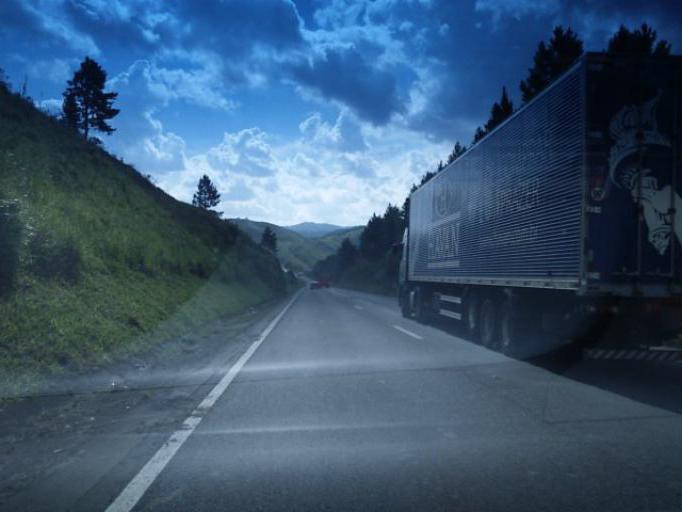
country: BR
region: Parana
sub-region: Campina Grande Do Sul
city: Campina Grande do Sul
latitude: -25.0998
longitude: -48.8174
